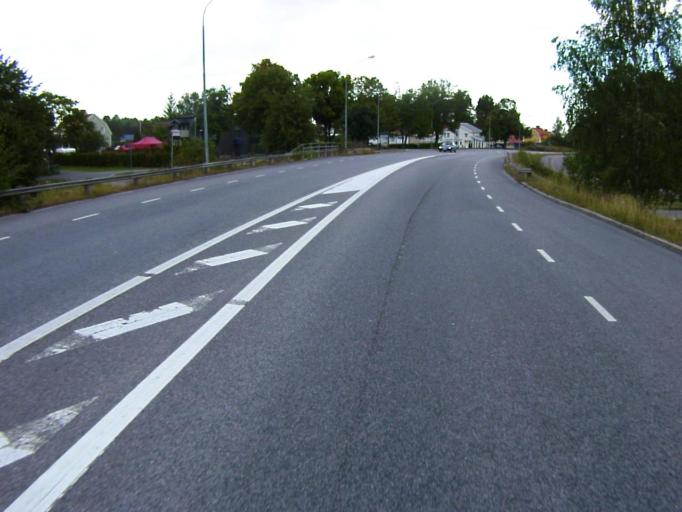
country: SE
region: Soedermanland
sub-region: Eskilstuna Kommun
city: Eskilstuna
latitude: 59.3930
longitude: 16.4937
